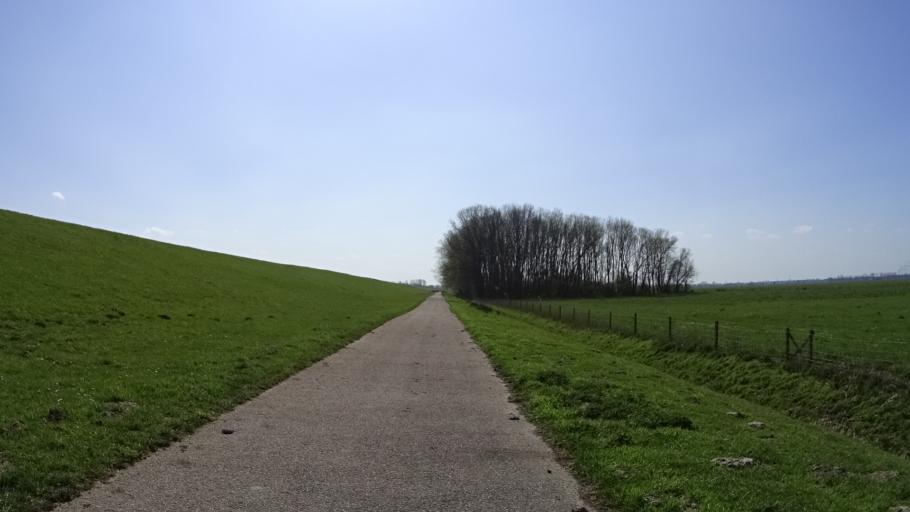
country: DE
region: Lower Saxony
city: Weener
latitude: 53.1470
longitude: 7.3701
